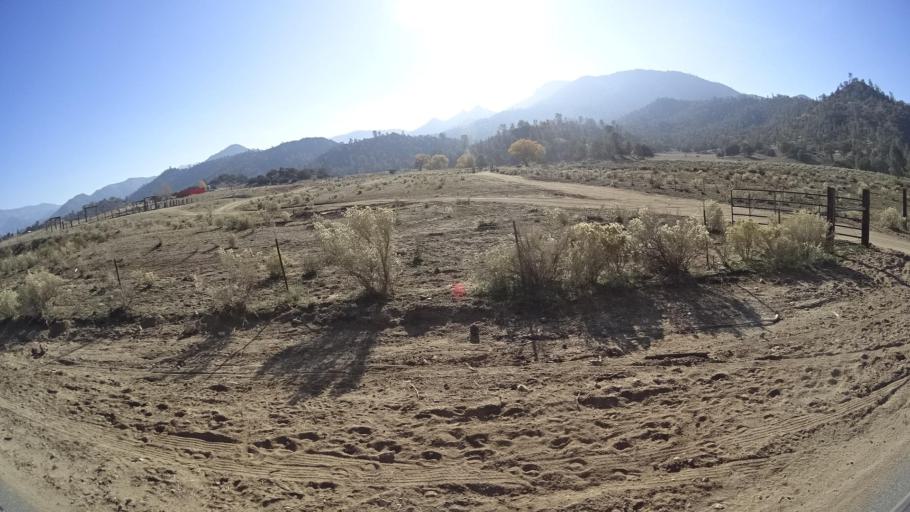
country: US
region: California
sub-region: Kern County
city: Tehachapi
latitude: 35.3157
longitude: -118.4000
